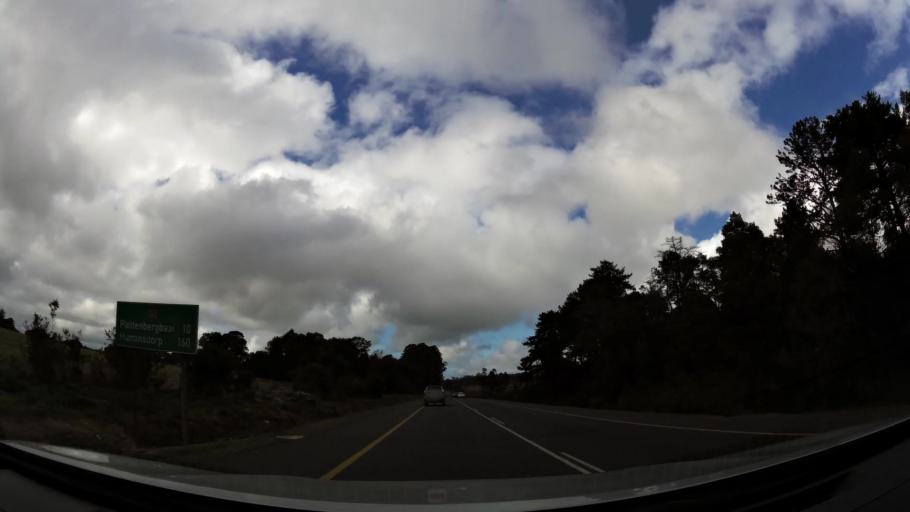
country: ZA
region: Western Cape
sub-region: Eden District Municipality
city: Plettenberg Bay
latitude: -34.0415
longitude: 23.2525
